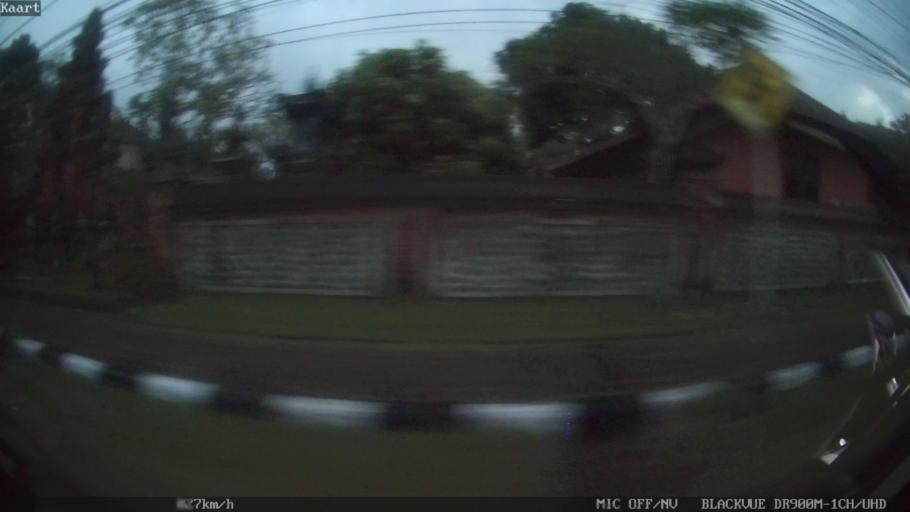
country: ID
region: Bali
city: Banjar Parekan
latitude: -8.5672
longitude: 115.2202
